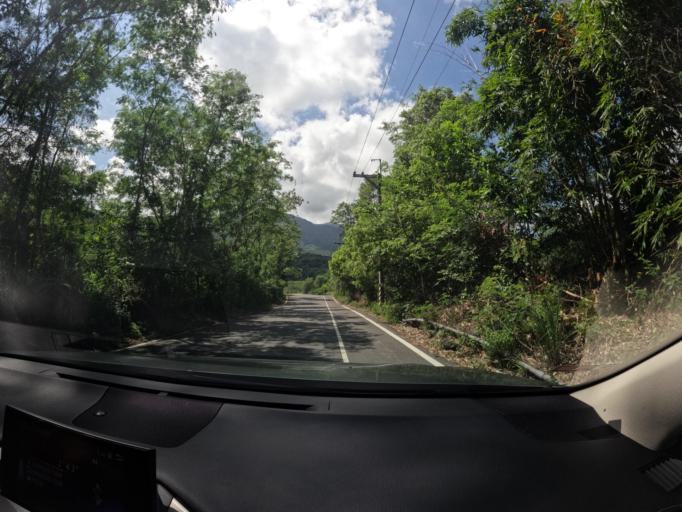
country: TW
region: Taiwan
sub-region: Hualien
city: Hualian
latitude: 23.6847
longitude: 121.4013
